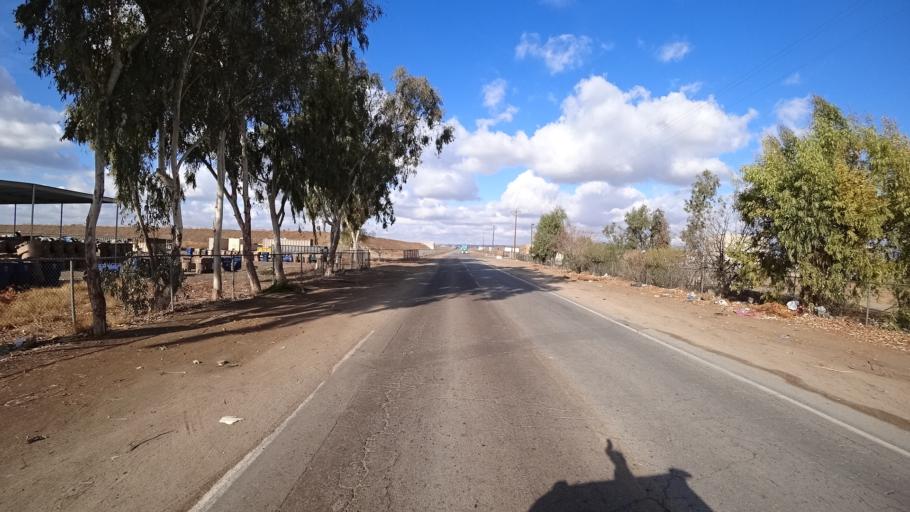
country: US
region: California
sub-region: Kern County
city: Greenfield
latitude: 35.3266
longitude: -118.9677
